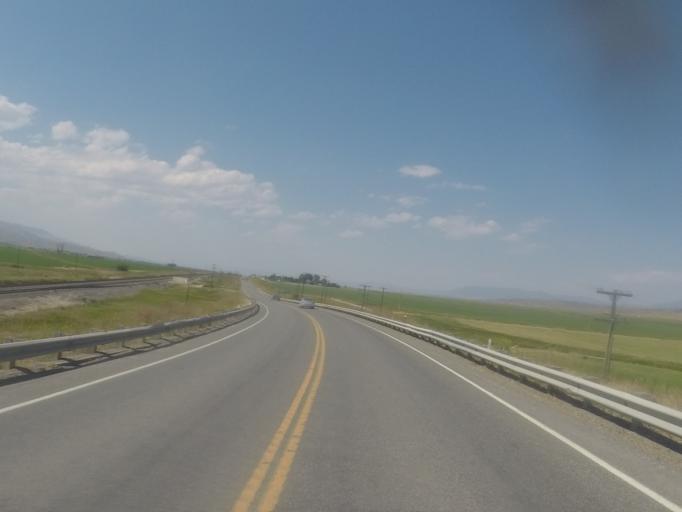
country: US
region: Montana
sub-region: Broadwater County
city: Townsend
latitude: 46.1788
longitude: -111.4441
